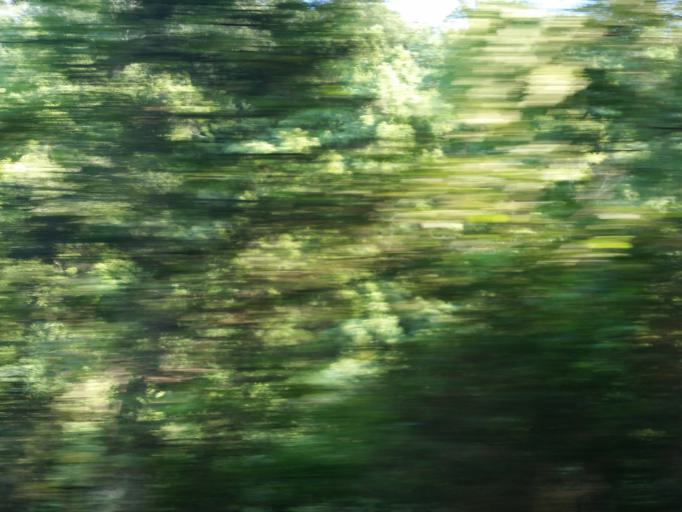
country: US
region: Tennessee
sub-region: Blount County
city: Eagleton Village
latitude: 35.8531
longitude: -83.9162
